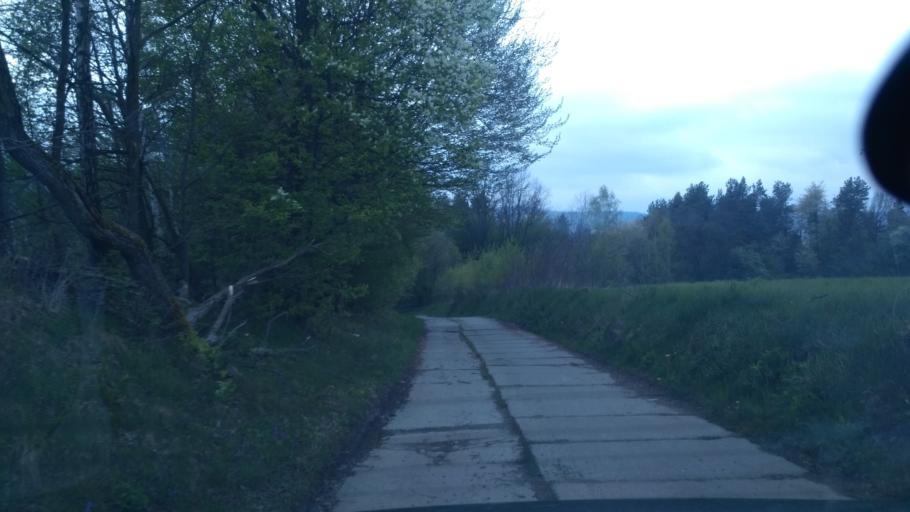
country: PL
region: Subcarpathian Voivodeship
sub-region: Powiat brzozowski
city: Dydnia
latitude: 49.6534
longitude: 22.2680
